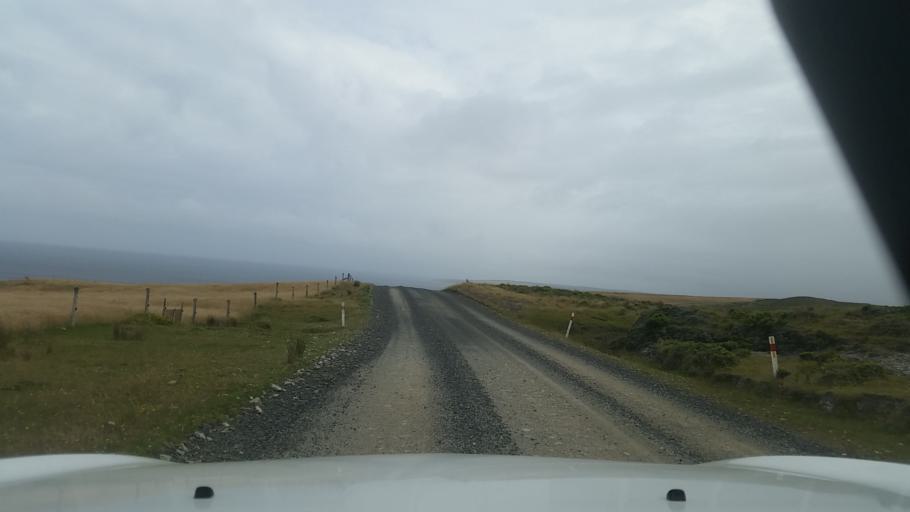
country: NZ
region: Chatham Islands
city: Waitangi
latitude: -43.8012
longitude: -176.6282
